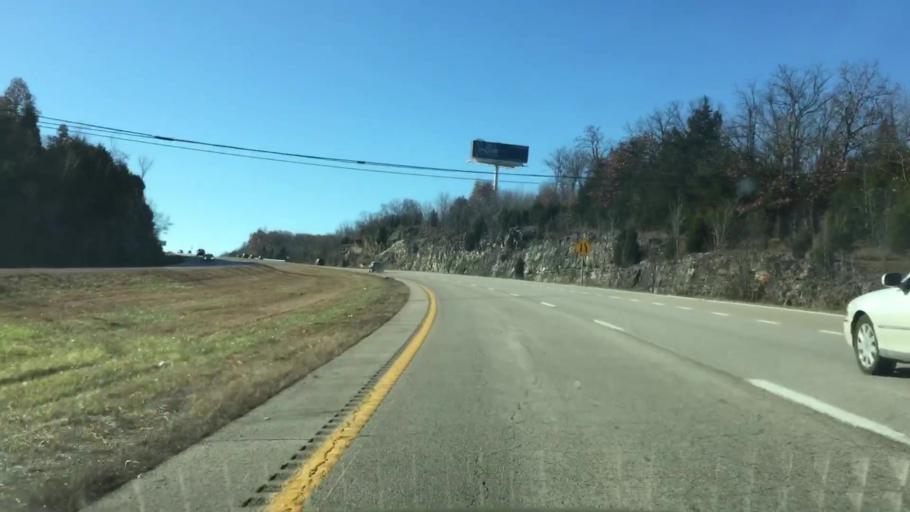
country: US
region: Missouri
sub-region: Cole County
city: Wardsville
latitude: 38.5027
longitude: -92.2663
